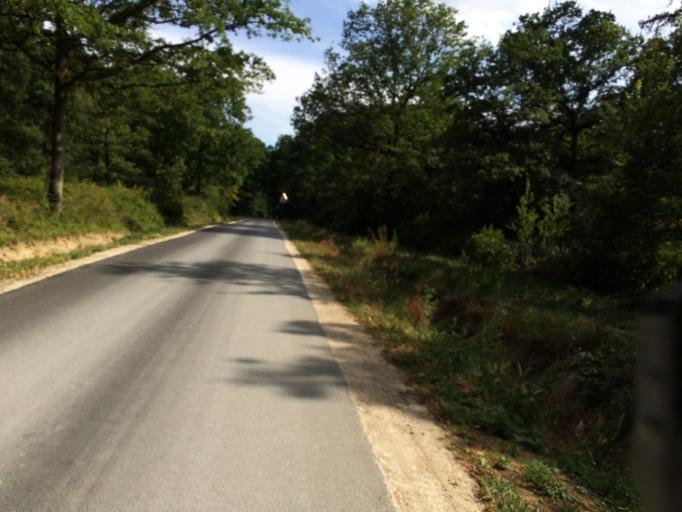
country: FR
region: Ile-de-France
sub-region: Departement de l'Essonne
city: Tigery
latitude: 48.6543
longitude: 2.4933
